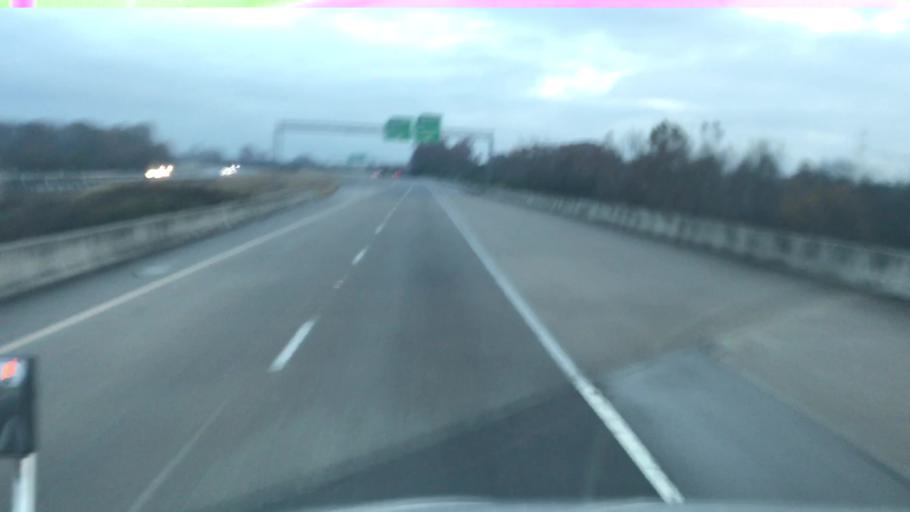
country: US
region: Tennessee
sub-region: Wilson County
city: Lebanon
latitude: 36.1748
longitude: -86.3519
